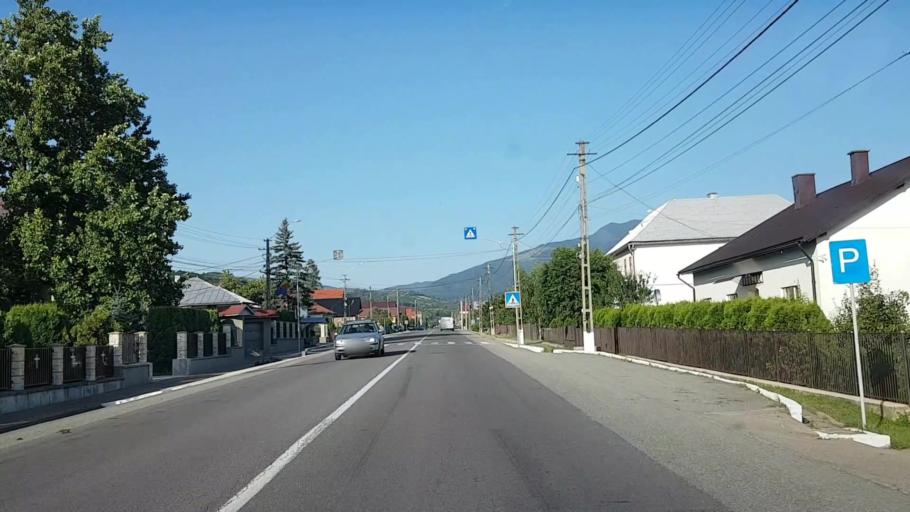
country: RO
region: Bistrita-Nasaud
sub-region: Comuna Tiha Bargaului
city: Tiha Bargaului
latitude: 47.2252
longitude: 24.7624
